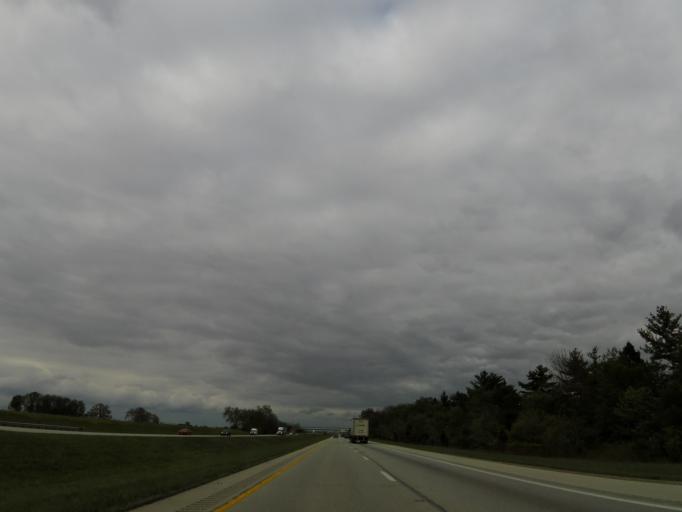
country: US
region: Ohio
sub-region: Clinton County
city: Wilmington
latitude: 39.5351
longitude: -83.7872
